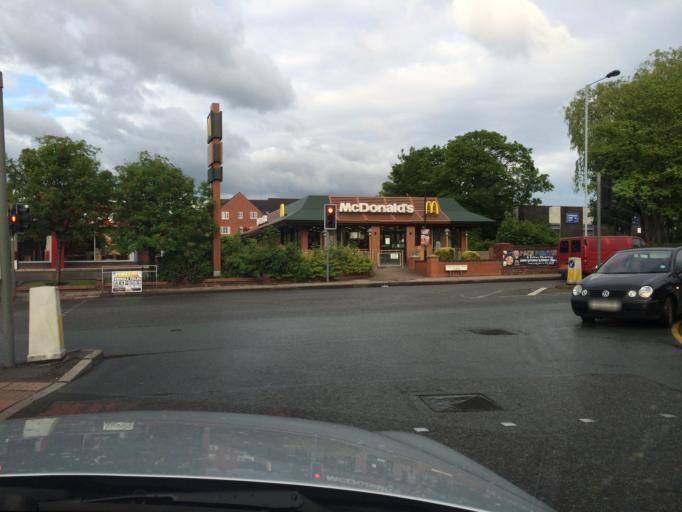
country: GB
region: England
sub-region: Manchester
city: Heaton Chapel
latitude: 53.4354
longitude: -2.1846
